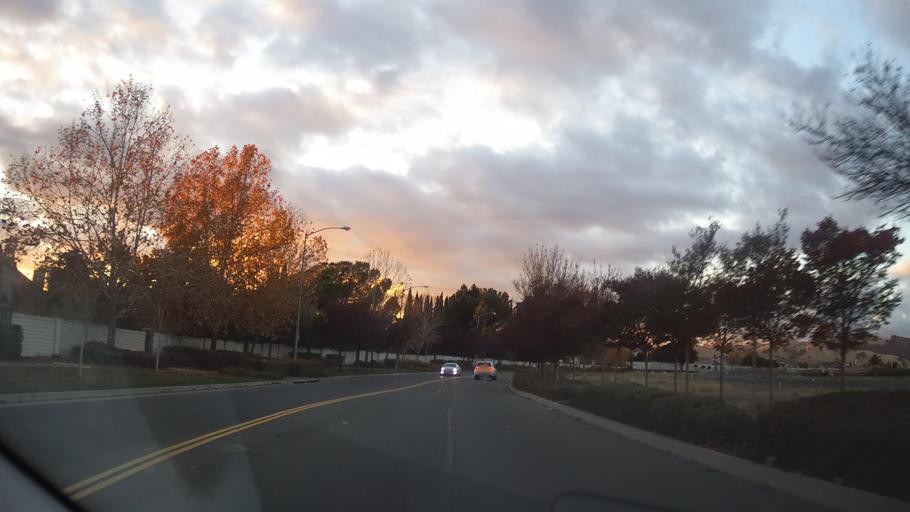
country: US
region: California
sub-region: Solano County
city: Fairfield
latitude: 38.2872
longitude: -122.0070
